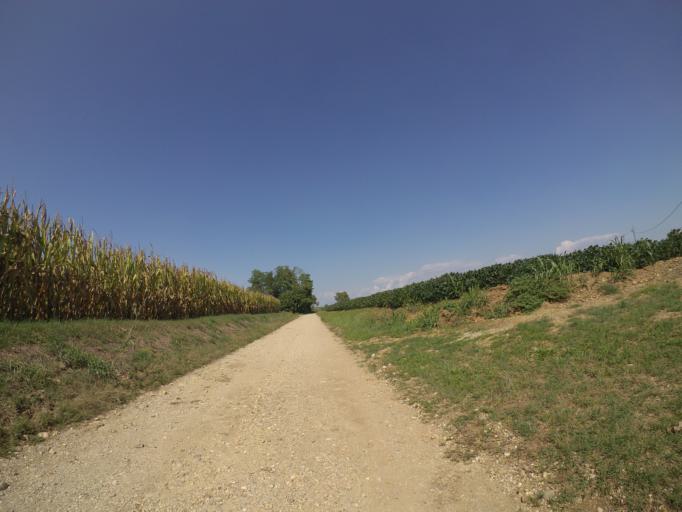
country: IT
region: Friuli Venezia Giulia
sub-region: Provincia di Udine
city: Bertiolo
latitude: 45.9418
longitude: 13.0690
